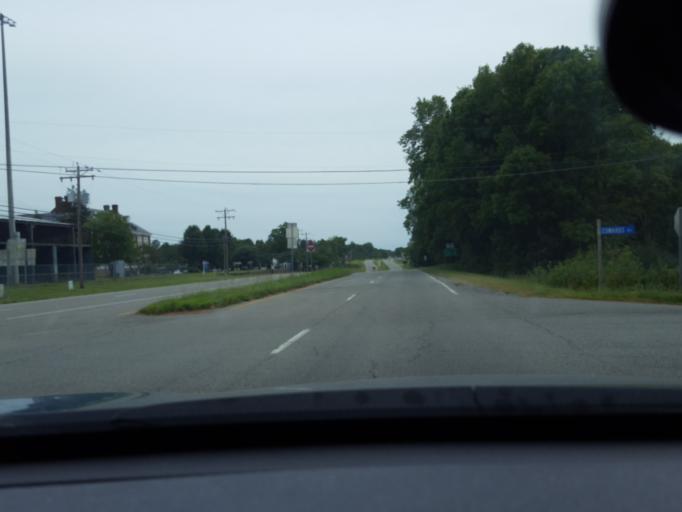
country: US
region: Virginia
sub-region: Caroline County
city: Bowling Green
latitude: 38.0401
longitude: -77.3437
